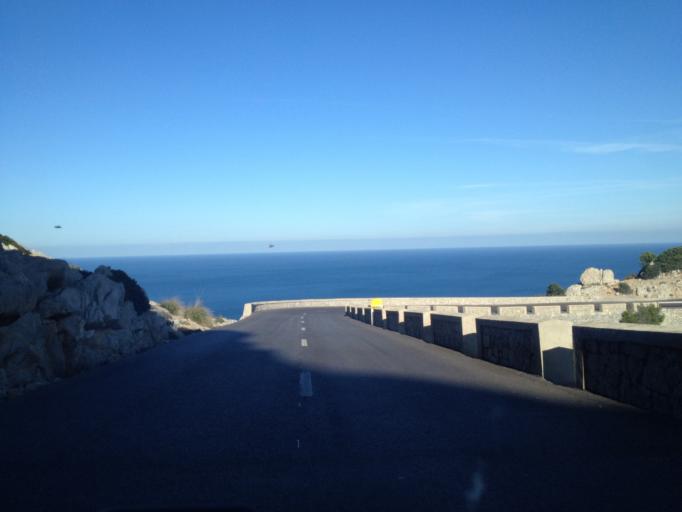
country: ES
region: Balearic Islands
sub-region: Illes Balears
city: Alcudia
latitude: 39.9595
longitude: 3.2101
